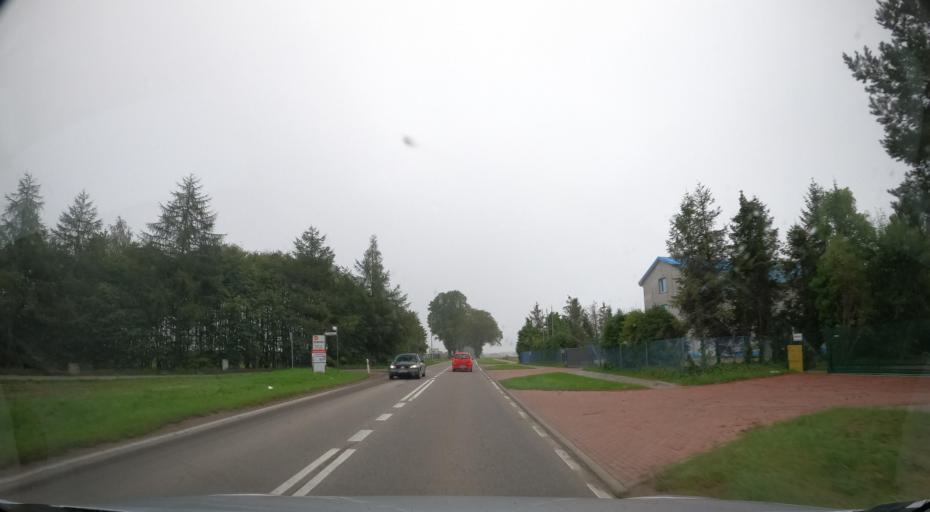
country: PL
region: Pomeranian Voivodeship
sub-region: Powiat wejherowski
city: Bojano
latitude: 54.4537
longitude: 18.3676
